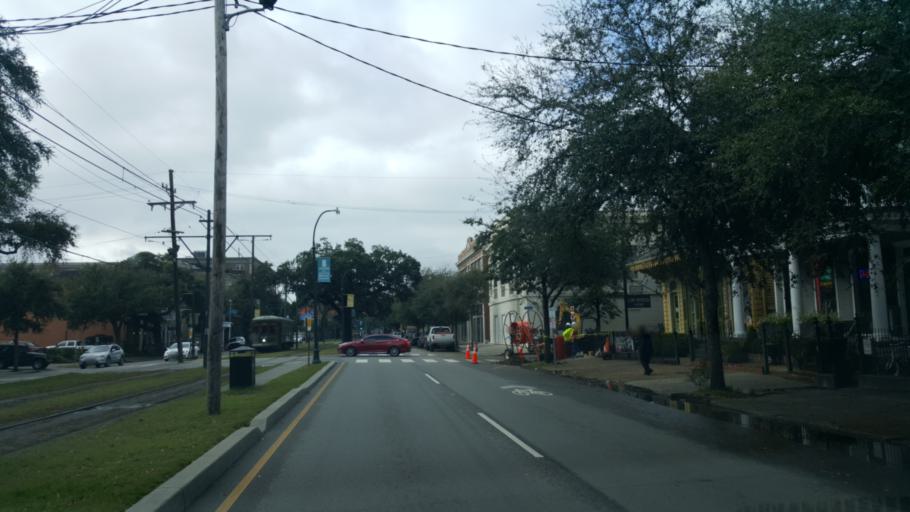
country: US
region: Louisiana
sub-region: Orleans Parish
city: New Orleans
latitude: 29.9381
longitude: -90.0763
